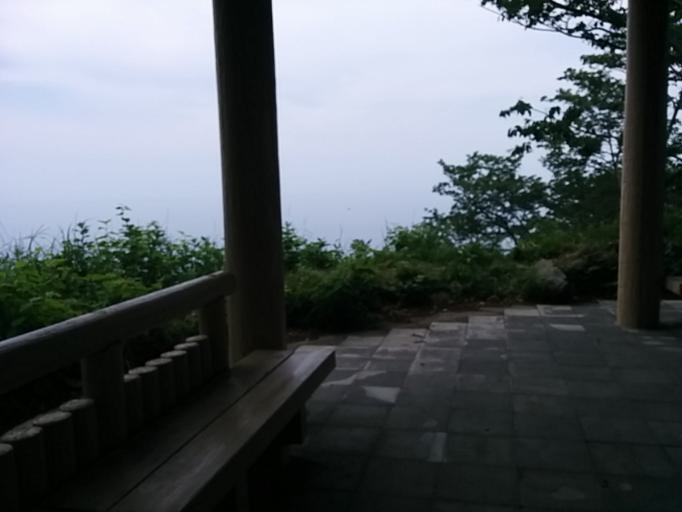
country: JP
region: Kyoto
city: Miyazu
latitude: 35.7752
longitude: 135.2230
